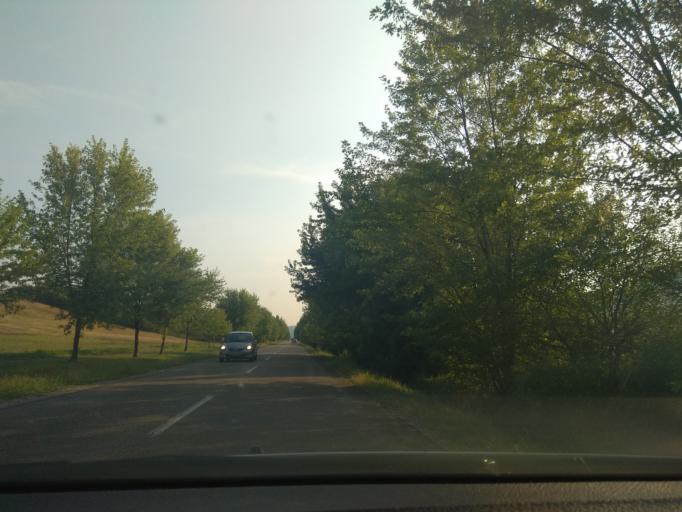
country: HU
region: Heves
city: Felsotarkany
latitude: 47.9508
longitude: 20.3868
